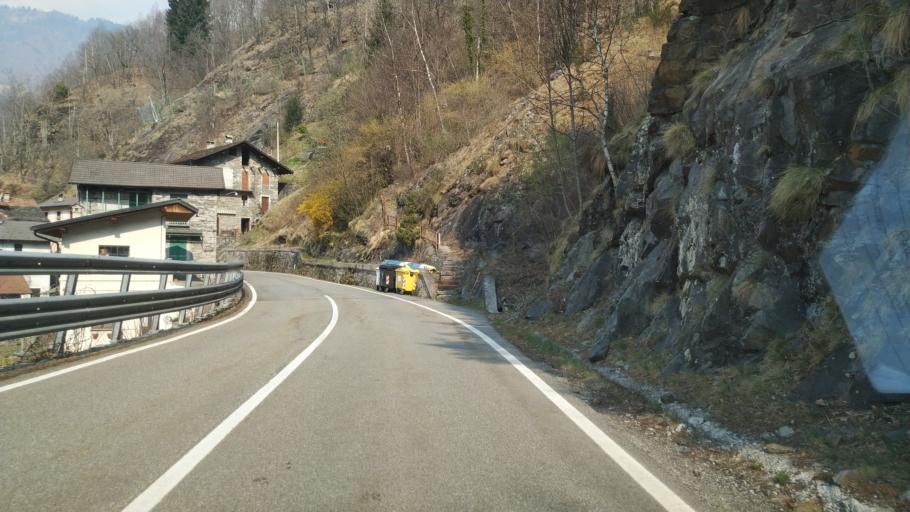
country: IT
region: Piedmont
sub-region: Provincia di Vercelli
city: Cravagliana
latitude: 45.8494
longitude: 8.1917
